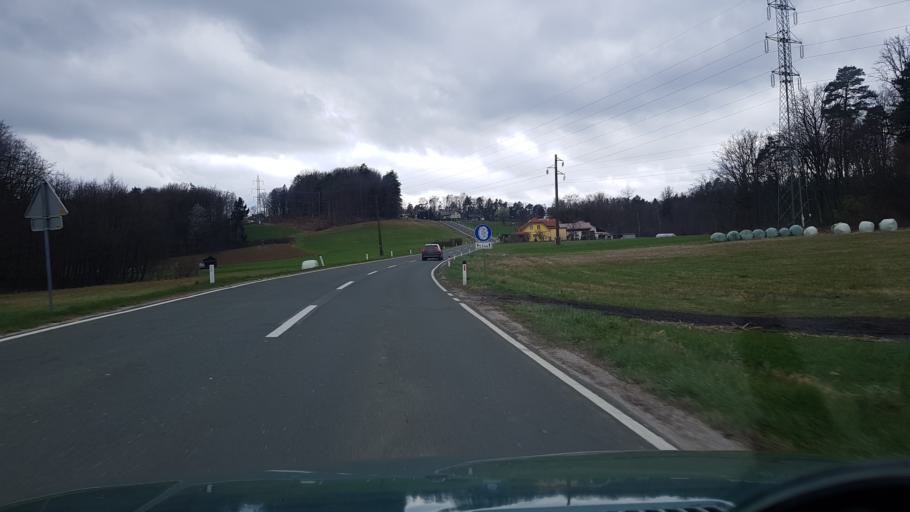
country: SI
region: Slovenska Bistrica
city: Slovenska Bistrica
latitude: 46.3731
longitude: 15.5342
